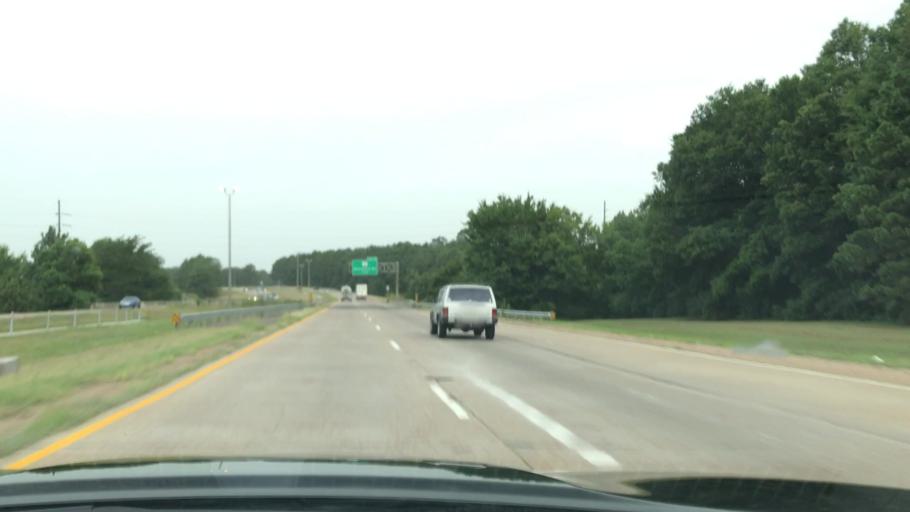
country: US
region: Louisiana
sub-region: Bossier Parish
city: Bossier City
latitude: 32.4206
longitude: -93.7697
